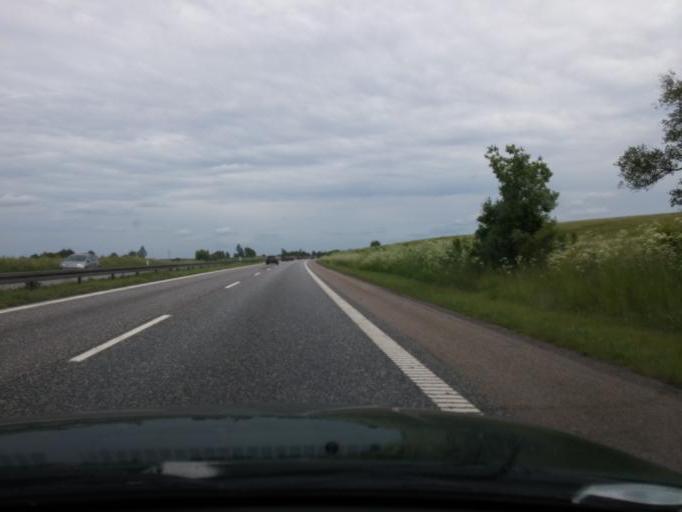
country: DK
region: South Denmark
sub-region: Odense Kommune
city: Bellinge
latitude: 55.3806
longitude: 10.2786
